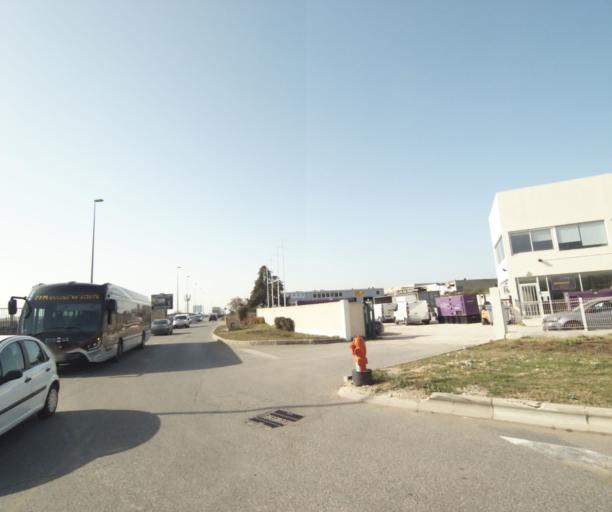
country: FR
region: Provence-Alpes-Cote d'Azur
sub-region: Departement des Bouches-du-Rhone
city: Saint-Victoret
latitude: 43.4312
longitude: 5.2407
